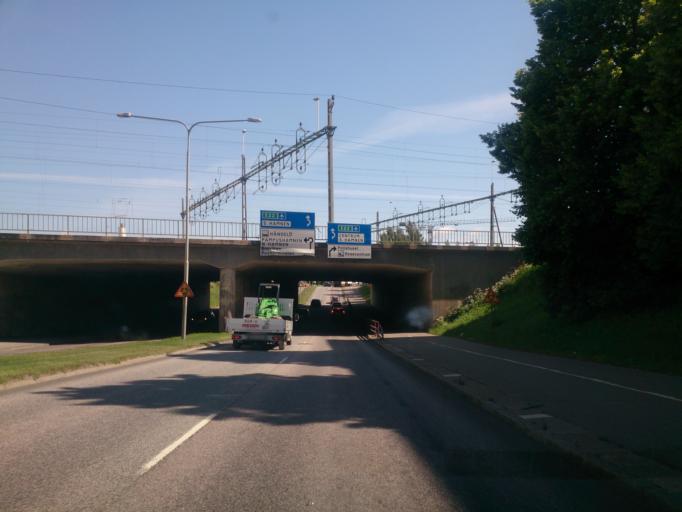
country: SE
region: OEstergoetland
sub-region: Norrkopings Kommun
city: Norrkoping
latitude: 58.5990
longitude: 16.1898
